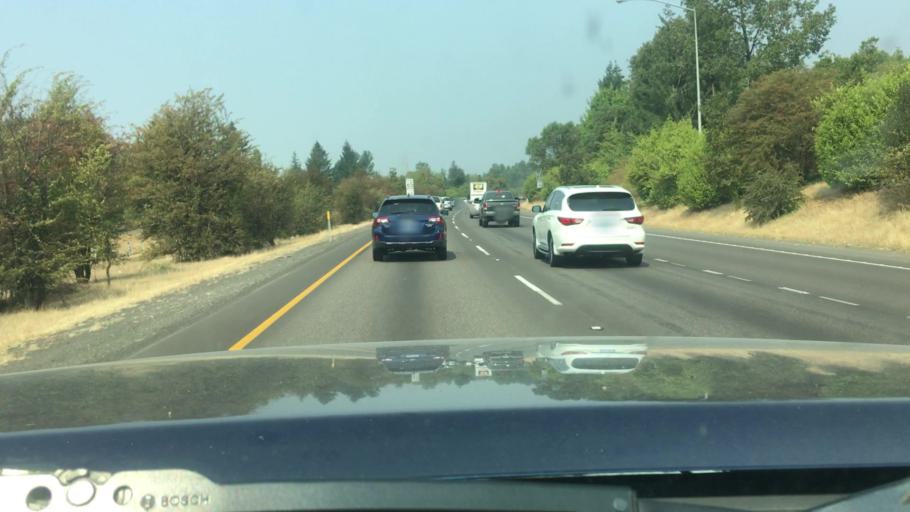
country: US
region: Oregon
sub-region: Clackamas County
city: West Linn
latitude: 45.3494
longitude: -122.6571
